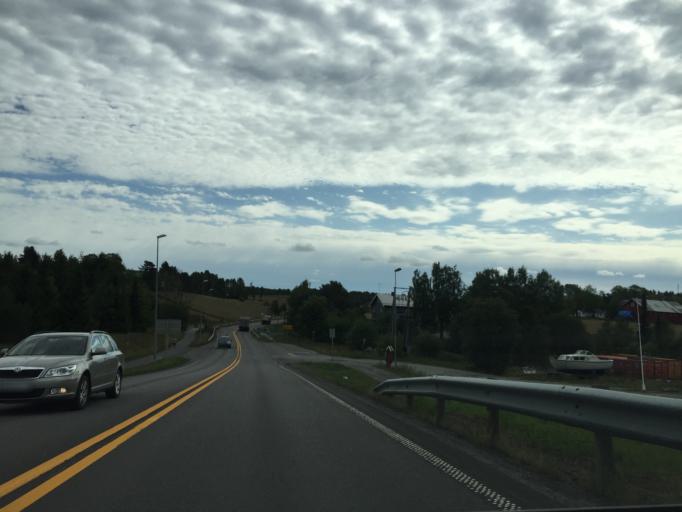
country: NO
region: Akershus
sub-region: Ski
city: Ski
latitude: 59.6727
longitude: 10.8866
